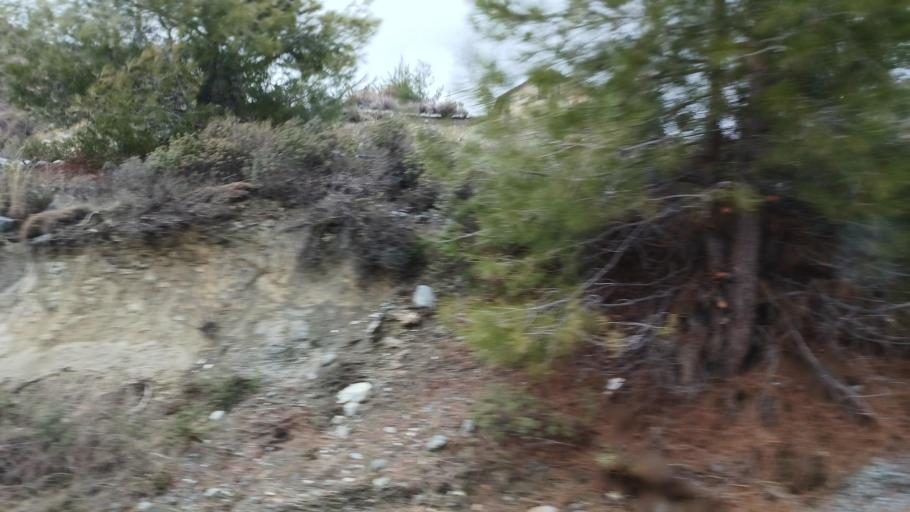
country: CY
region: Limassol
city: Kyperounta
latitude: 34.9340
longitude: 32.9766
